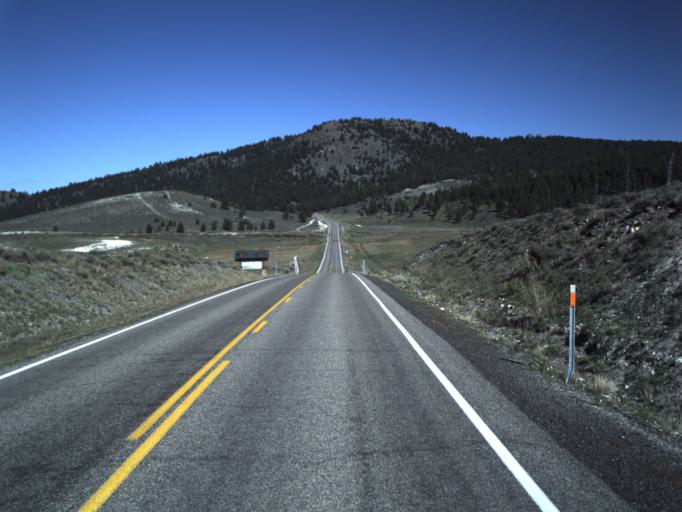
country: US
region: Utah
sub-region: Iron County
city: Parowan
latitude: 37.7045
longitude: -112.6429
